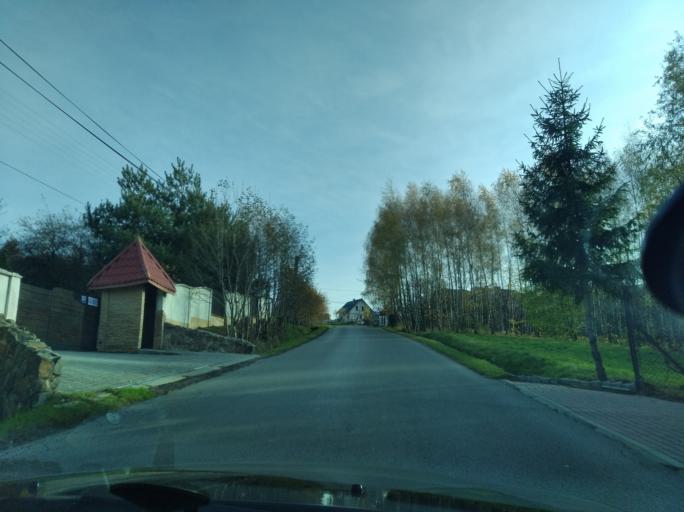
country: PL
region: Subcarpathian Voivodeship
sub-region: Powiat rzeszowski
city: Tyczyn
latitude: 49.9936
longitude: 22.0664
